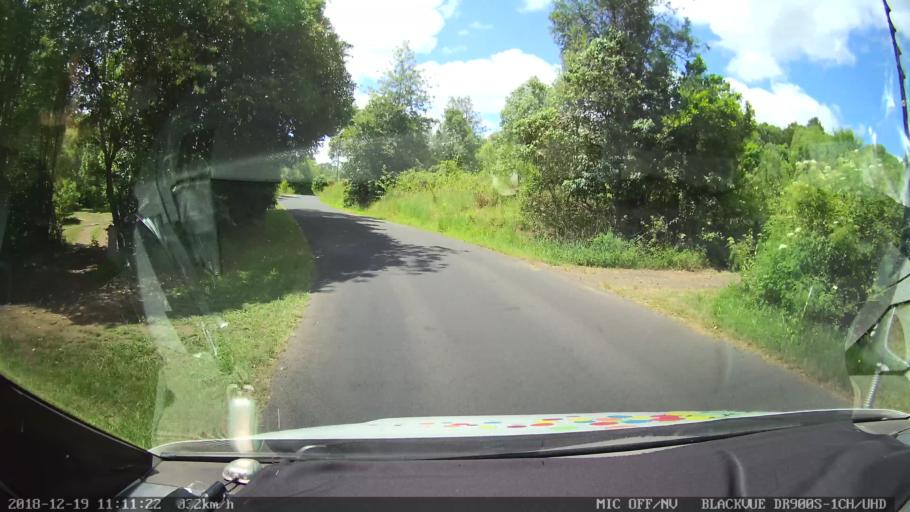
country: AU
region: New South Wales
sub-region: Lismore Municipality
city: Nimbin
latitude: -28.6428
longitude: 153.2579
